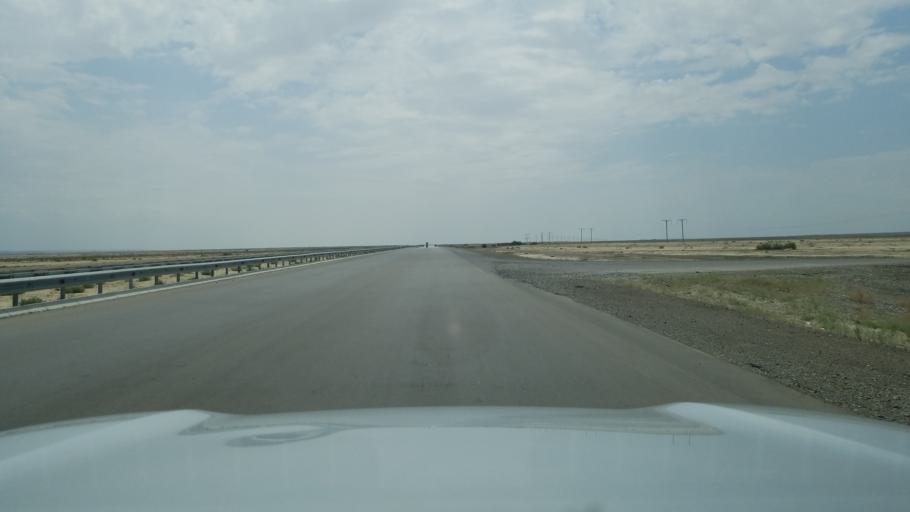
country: TM
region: Balkan
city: Gazanjyk
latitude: 39.2357
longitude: 55.0784
